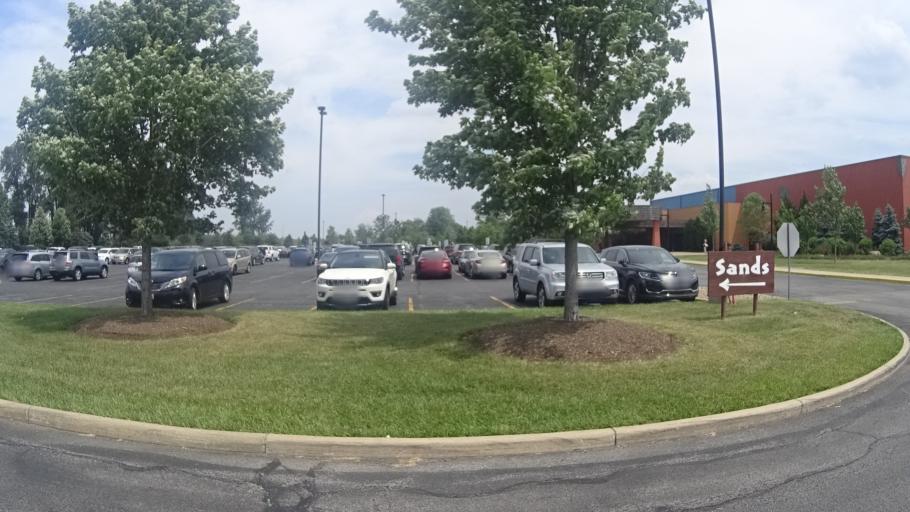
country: US
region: Ohio
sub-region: Erie County
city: Huron
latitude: 41.3861
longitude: -82.6421
